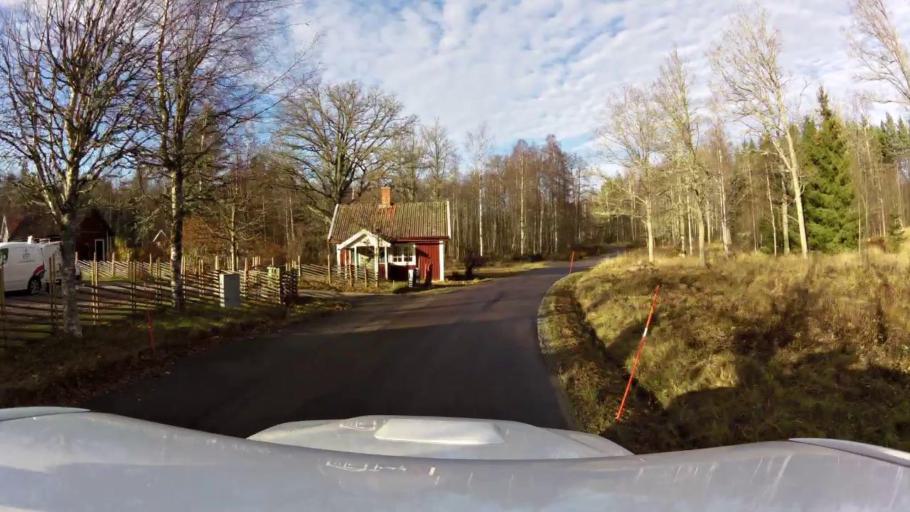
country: SE
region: OEstergoetland
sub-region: Linkopings Kommun
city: Sturefors
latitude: 58.2594
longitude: 15.6927
